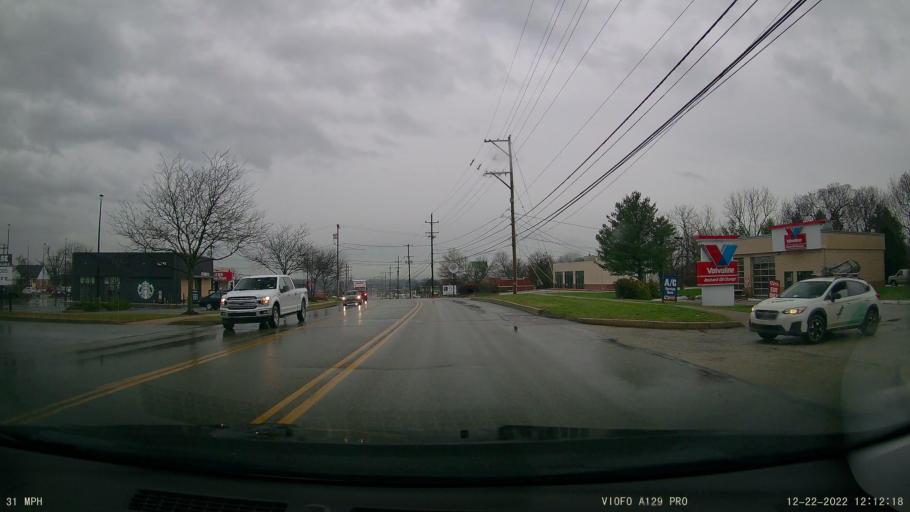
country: US
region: Pennsylvania
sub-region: Montgomery County
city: Trooper
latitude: 40.1460
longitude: -75.3946
